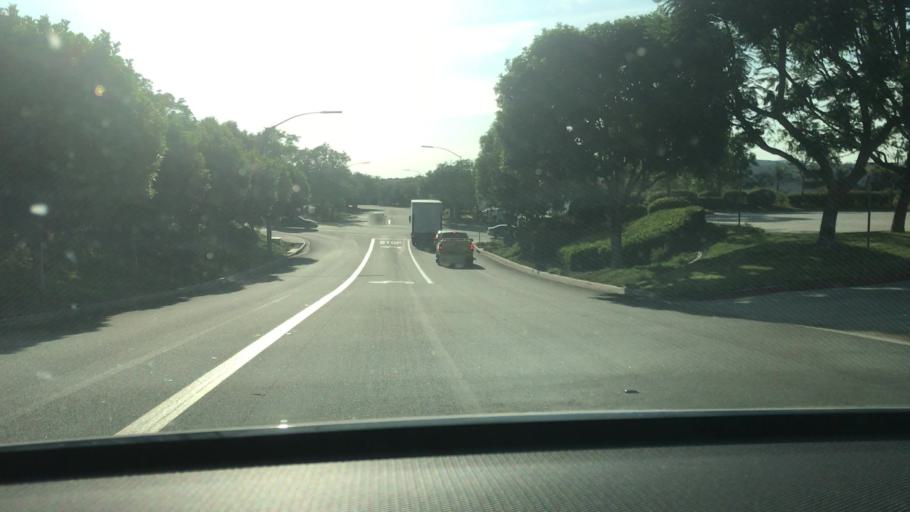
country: US
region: California
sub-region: San Diego County
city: Poway
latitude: 32.9404
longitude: -117.0444
